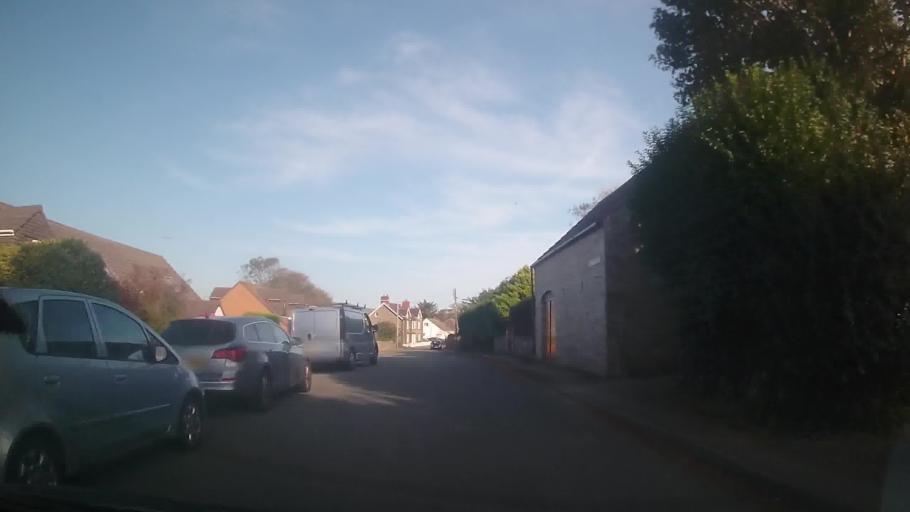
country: GB
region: Wales
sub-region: Pembrokeshire
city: Fishguard
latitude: 51.9922
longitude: -4.9716
